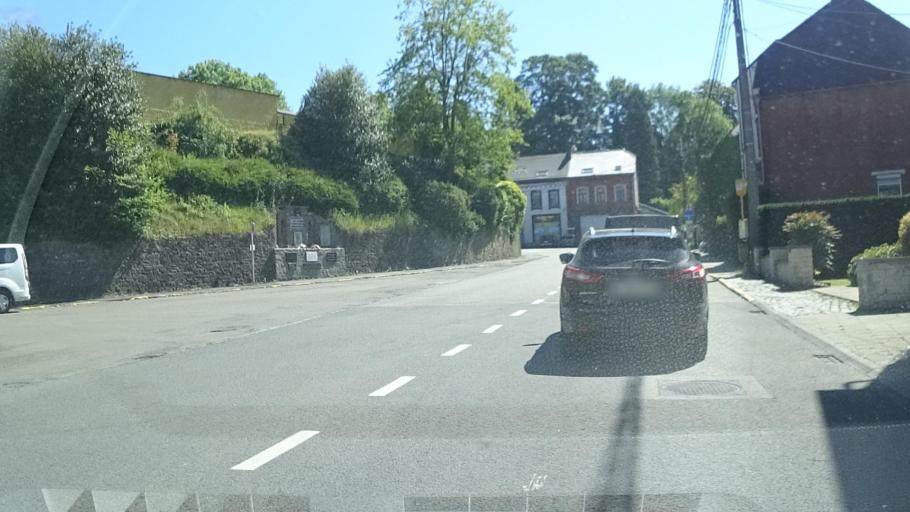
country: BE
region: Wallonia
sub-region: Province du Brabant Wallon
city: Court-Saint-Etienne
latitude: 50.6438
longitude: 4.5678
